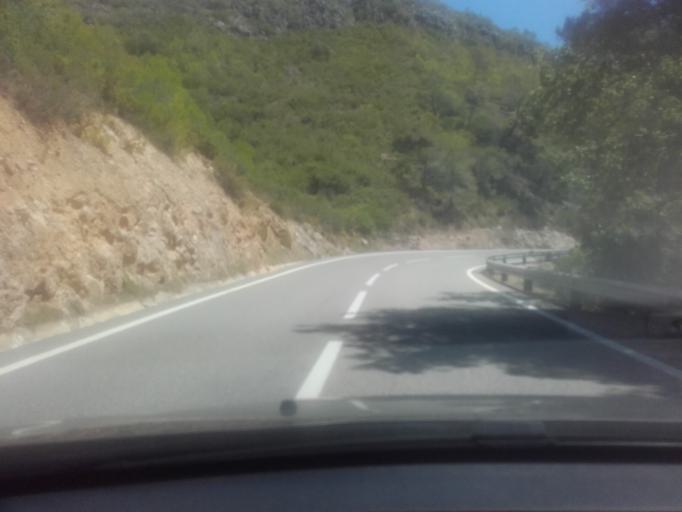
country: ES
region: Catalonia
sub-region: Provincia de Tarragona
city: la Bisbal del Penedes
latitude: 41.2983
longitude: 1.4816
